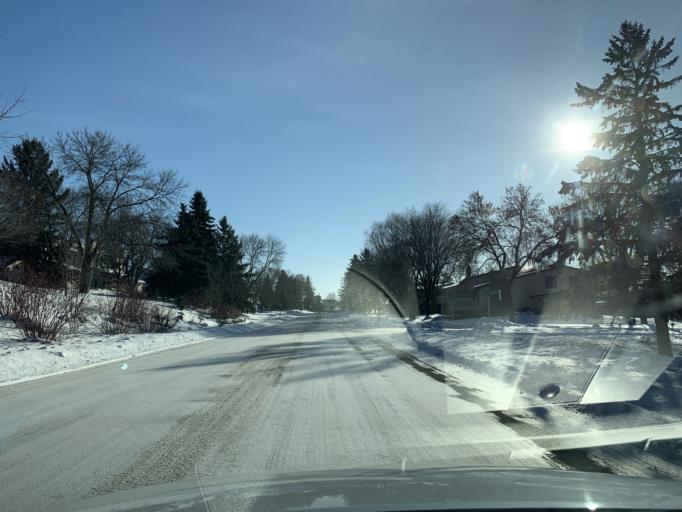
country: US
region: Minnesota
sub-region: Scott County
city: Savage
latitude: 44.8283
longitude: -93.3529
